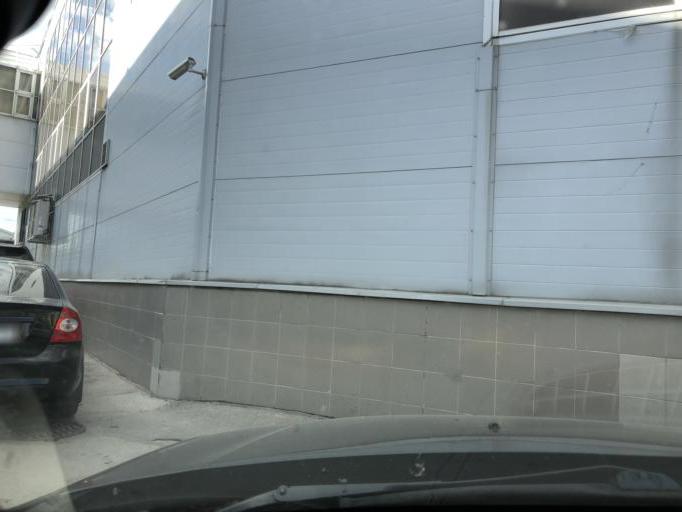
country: RU
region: Tula
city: Tula
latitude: 54.1977
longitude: 37.5816
